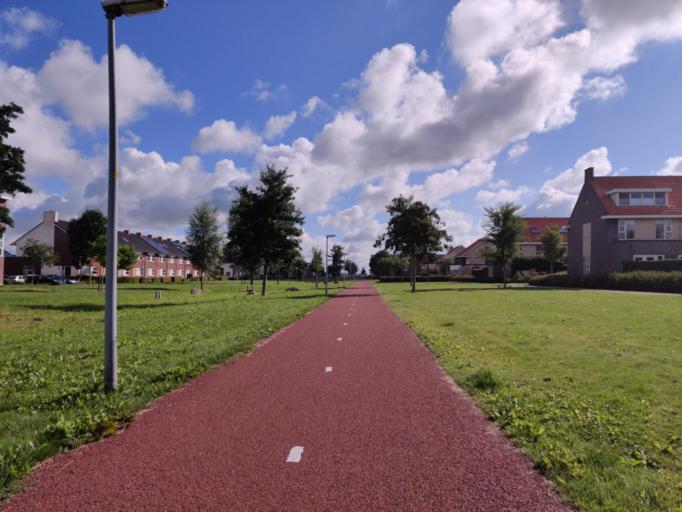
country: NL
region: Flevoland
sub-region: Gemeente Zeewolde
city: Zeewolde
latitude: 52.3441
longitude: 5.5208
